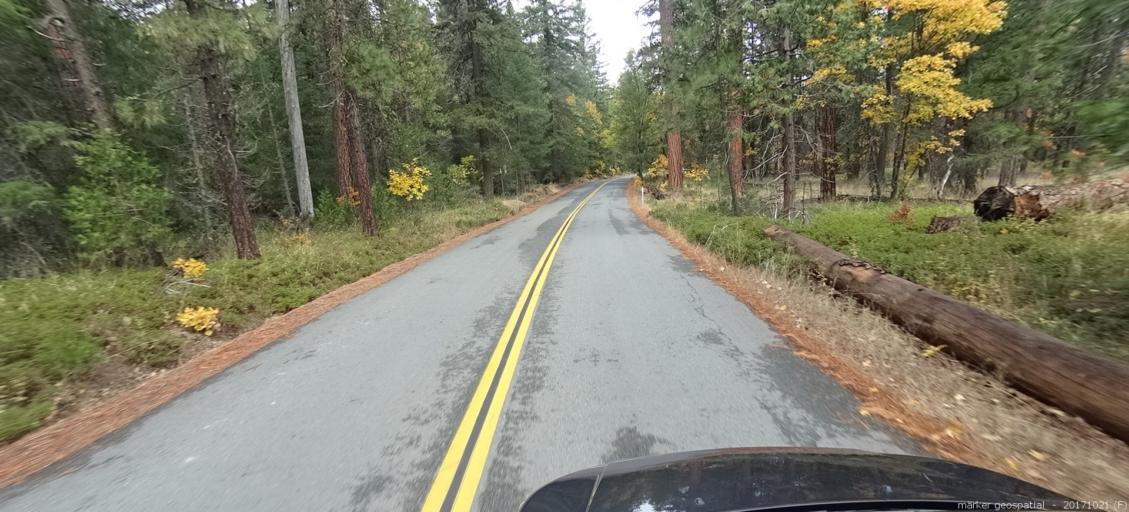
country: US
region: California
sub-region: Shasta County
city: Burney
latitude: 41.0095
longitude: -121.6539
